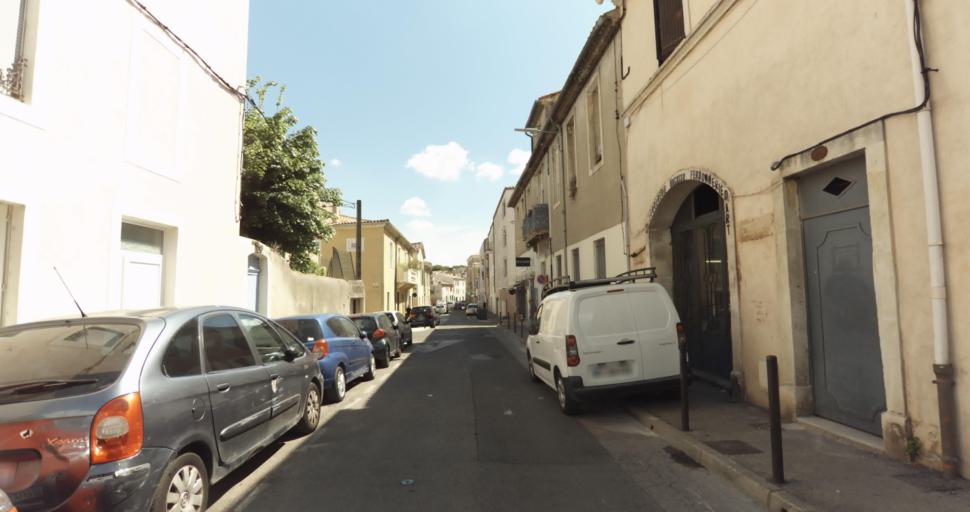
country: FR
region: Languedoc-Roussillon
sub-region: Departement du Gard
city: Nimes
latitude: 43.8427
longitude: 4.3610
